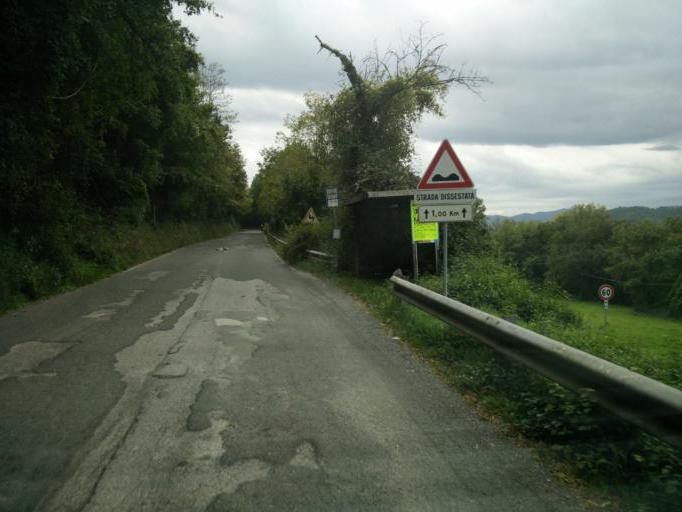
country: IT
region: Tuscany
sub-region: Provincia di Massa-Carrara
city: Fivizzano
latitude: 44.2111
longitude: 10.0914
